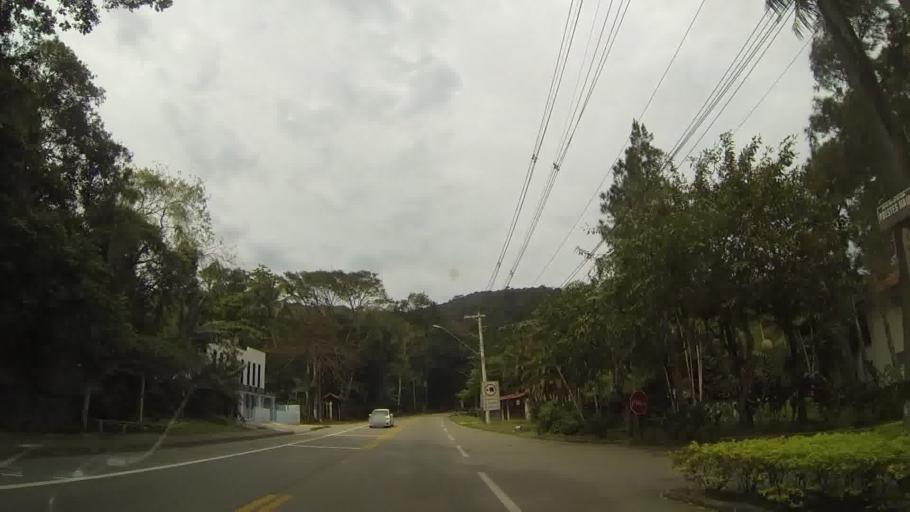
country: BR
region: Sao Paulo
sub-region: Sao Sebastiao
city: Sao Sebastiao
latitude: -23.8152
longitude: -45.5278
